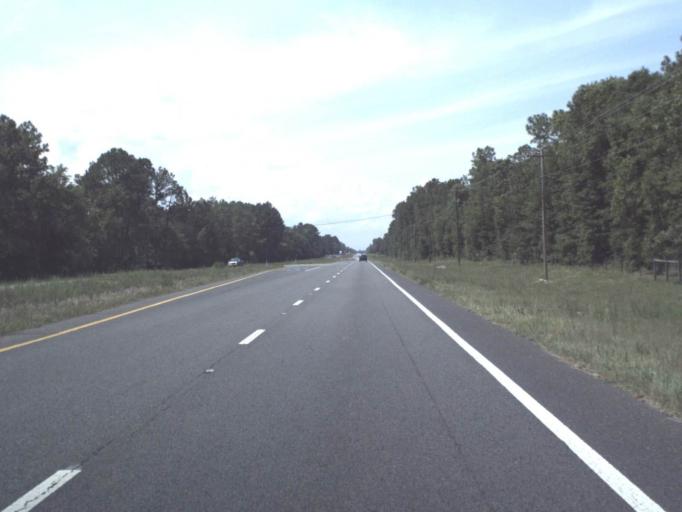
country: US
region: Florida
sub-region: Clay County
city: Green Cove Springs
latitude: 29.8928
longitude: -81.6699
